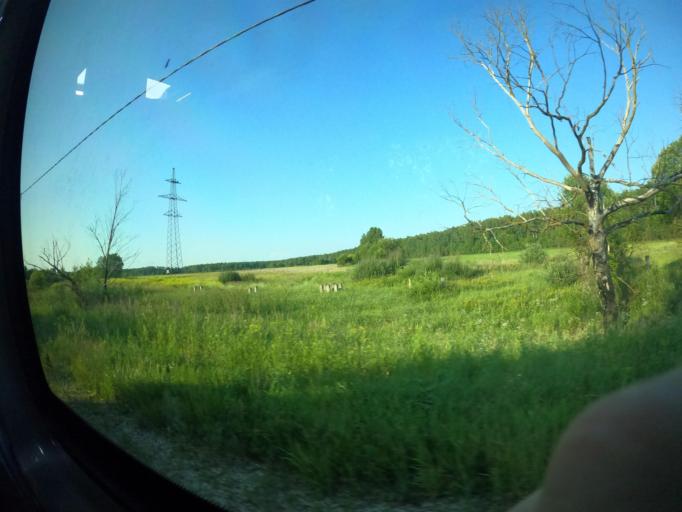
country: RU
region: Moskovskaya
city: Obolensk
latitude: 54.9304
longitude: 37.2526
